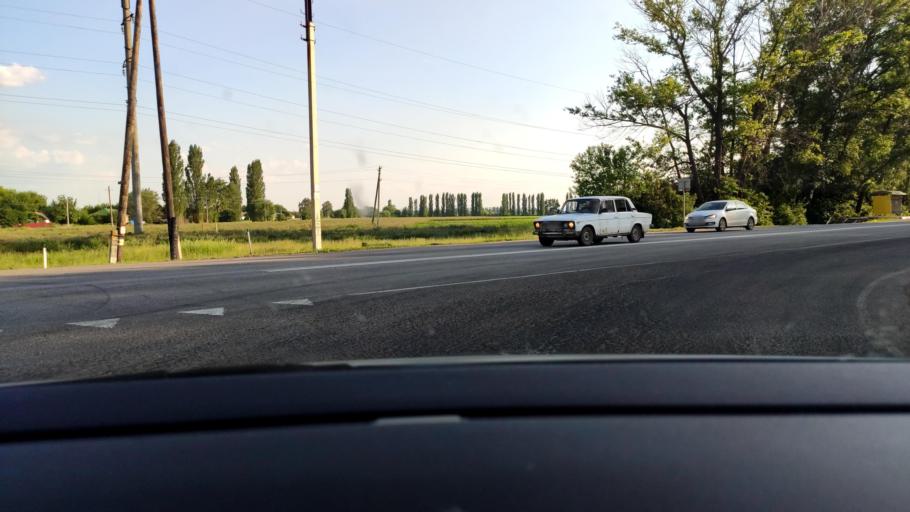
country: RU
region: Voronezj
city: Kashirskoye
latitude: 51.4672
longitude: 39.8633
